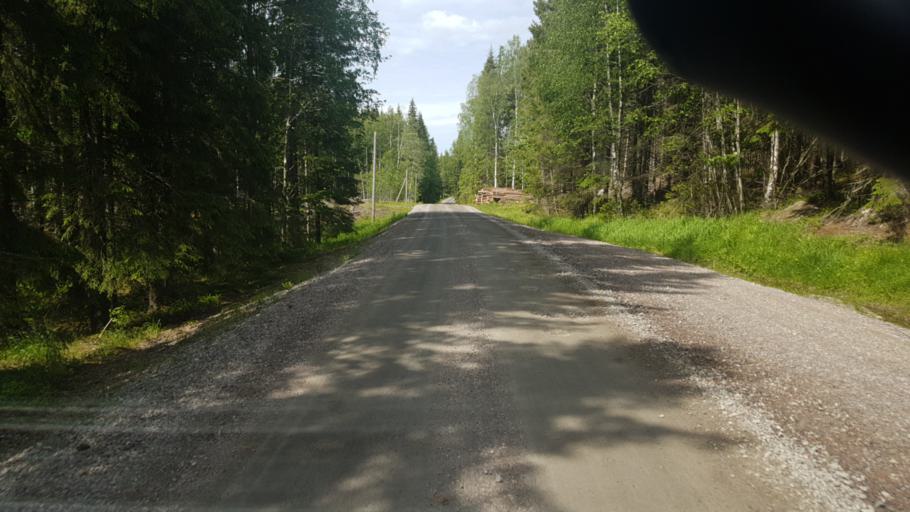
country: SE
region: Vaermland
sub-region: Eda Kommun
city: Charlottenberg
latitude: 59.9870
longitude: 12.4838
